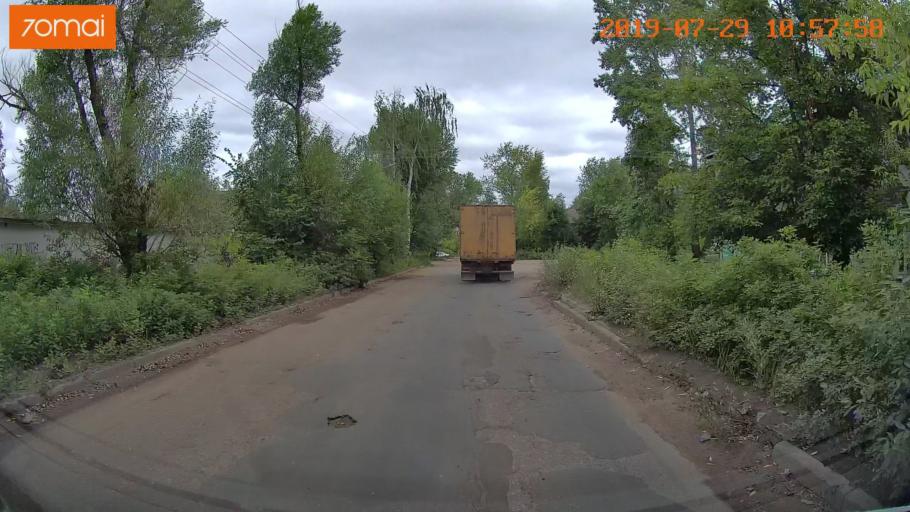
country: RU
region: Ivanovo
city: Bogorodskoye
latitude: 56.9916
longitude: 41.0378
